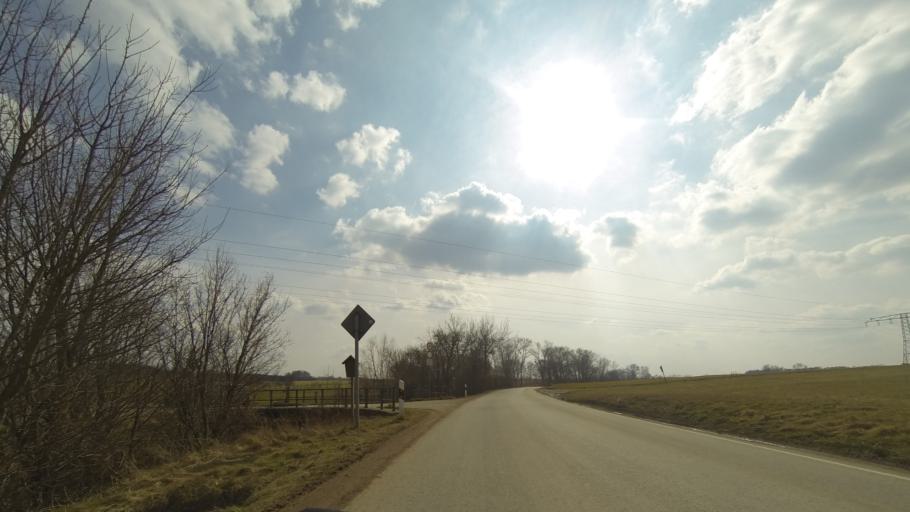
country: DE
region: Saxony
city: Moritzburg
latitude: 51.1436
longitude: 13.7414
